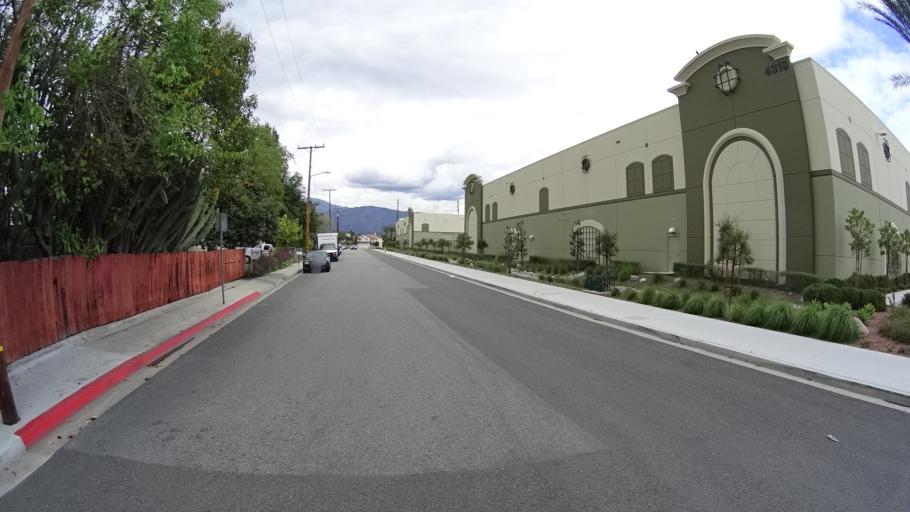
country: US
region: California
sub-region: Los Angeles County
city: Baldwin Park
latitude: 34.0906
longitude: -117.9548
